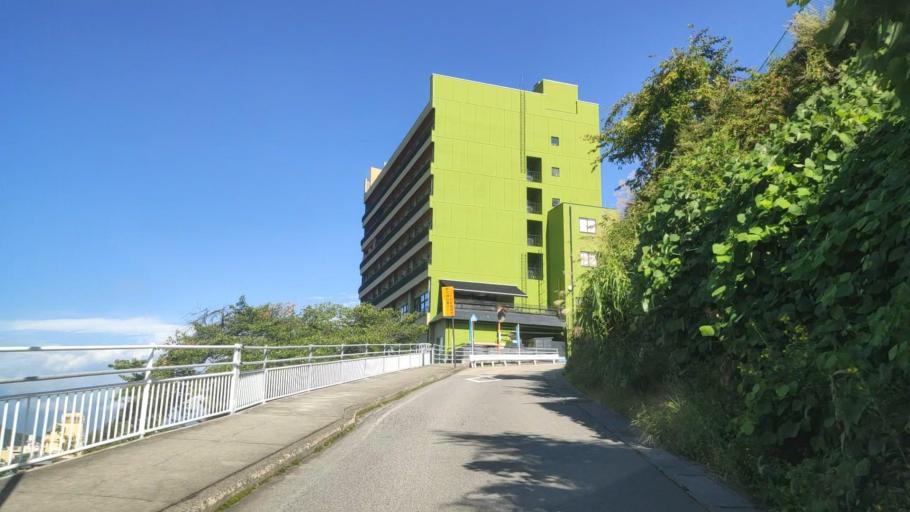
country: JP
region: Nagano
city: Nakano
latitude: 36.7379
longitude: 138.4205
